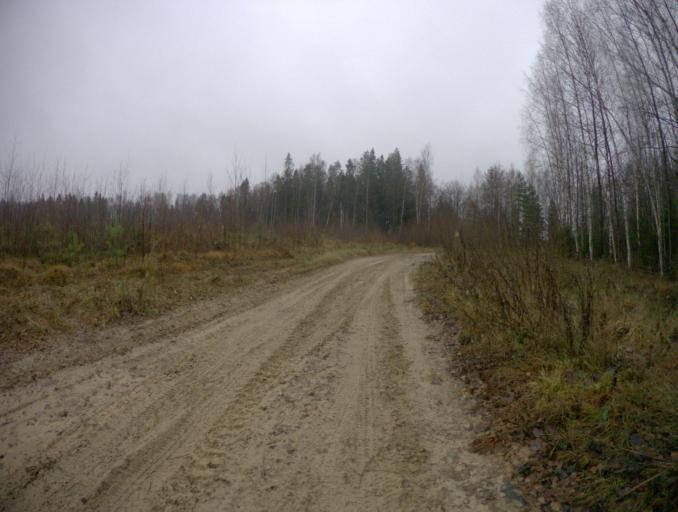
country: RU
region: Vladimir
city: Golovino
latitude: 55.9908
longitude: 40.4474
